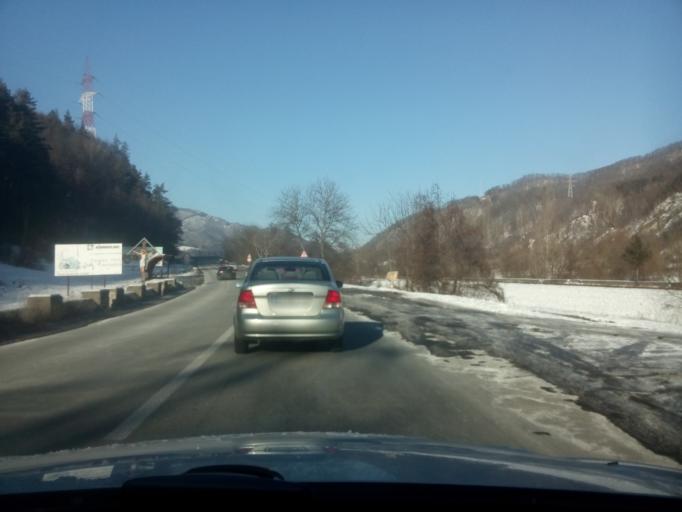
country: RO
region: Valcea
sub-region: Comuna Brezoi
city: Brezoi
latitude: 45.3566
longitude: 24.2970
